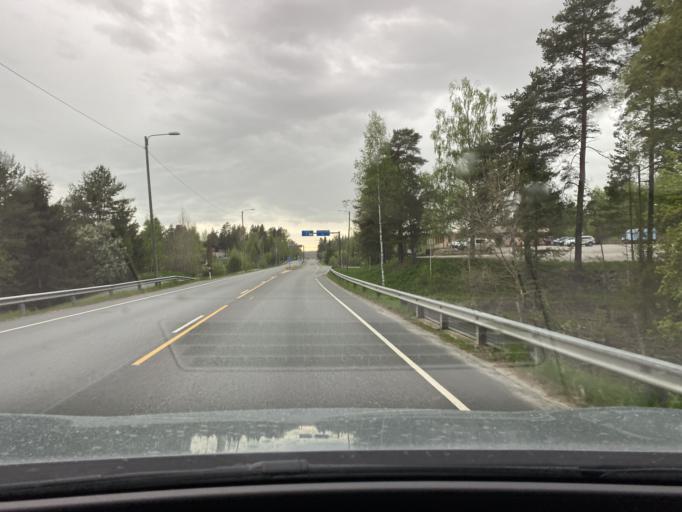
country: FI
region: Varsinais-Suomi
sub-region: Salo
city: Suomusjaervi
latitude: 60.3776
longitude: 23.5981
